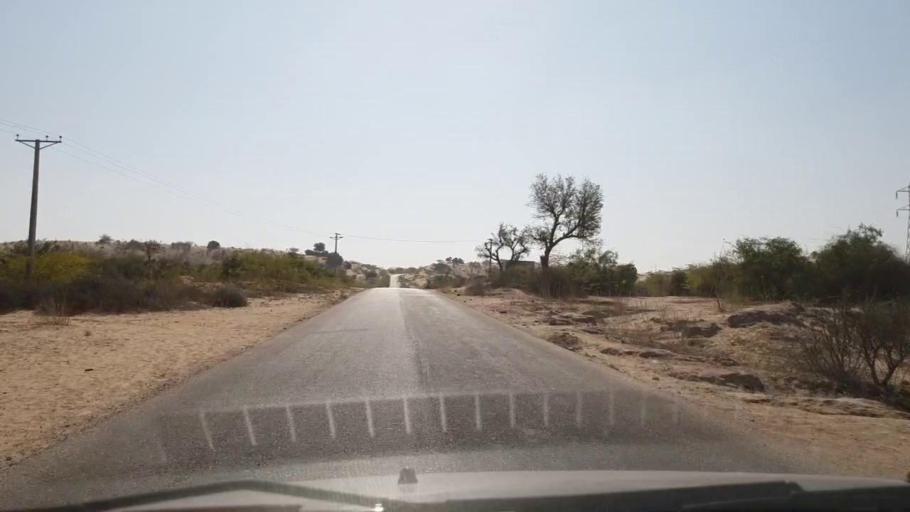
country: PK
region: Sindh
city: Mithi
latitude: 24.5950
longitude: 69.7133
